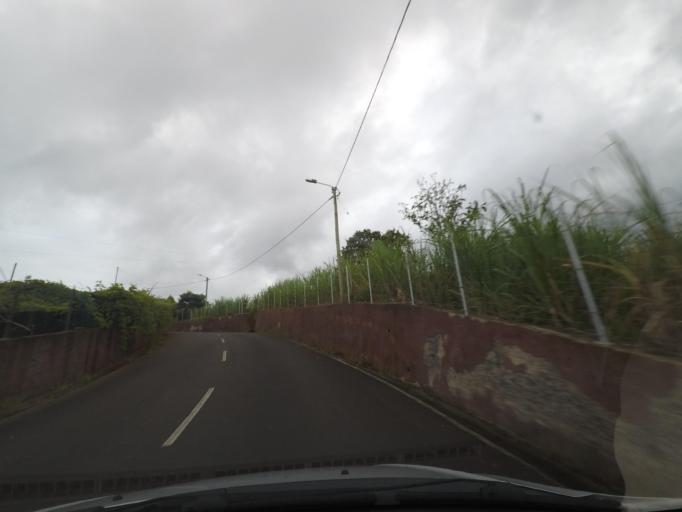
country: PT
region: Madeira
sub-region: Santana
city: Santana
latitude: 32.8185
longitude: -16.8847
